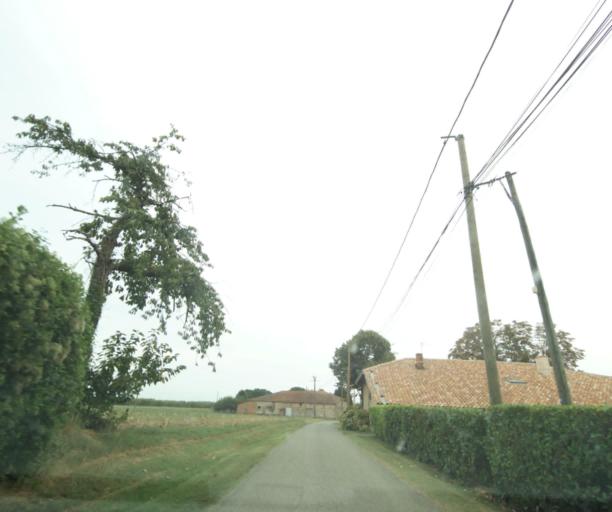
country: FR
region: Midi-Pyrenees
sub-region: Departement du Tarn-et-Garonne
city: Saint-Porquier
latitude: 43.9728
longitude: 1.1873
